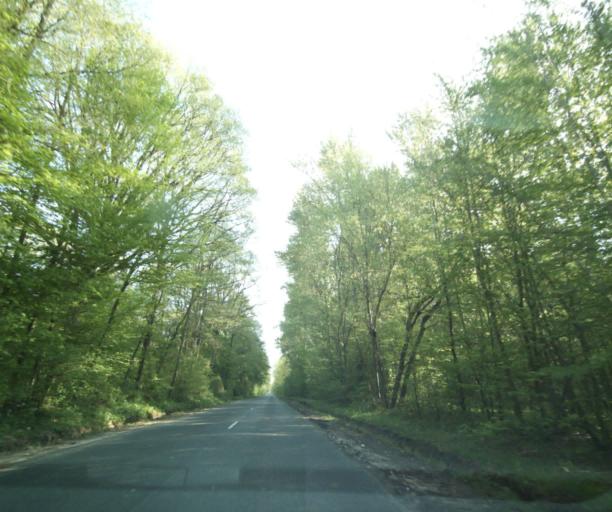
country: FR
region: Ile-de-France
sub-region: Departement de Seine-et-Marne
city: Vernou-la-Celle-sur-Seine
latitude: 48.4119
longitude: 2.8409
